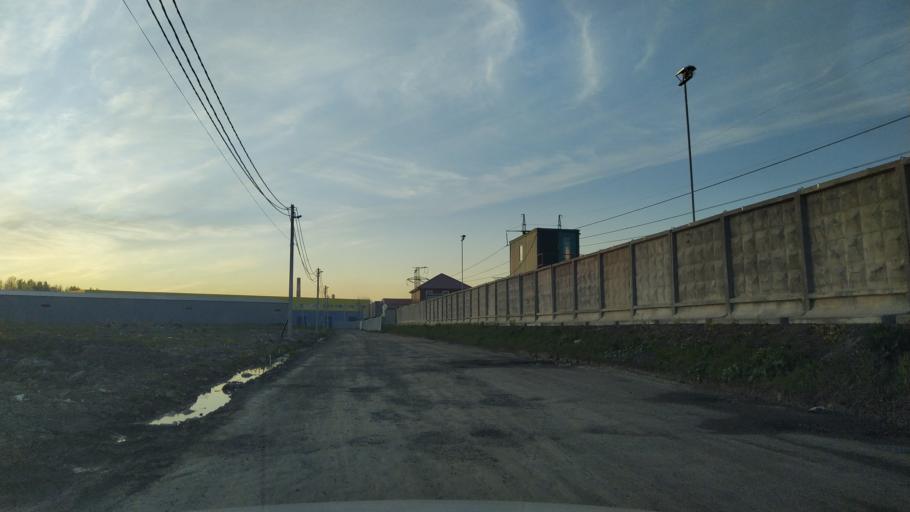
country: RU
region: St.-Petersburg
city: Obukhovo
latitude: 59.8042
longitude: 30.4598
